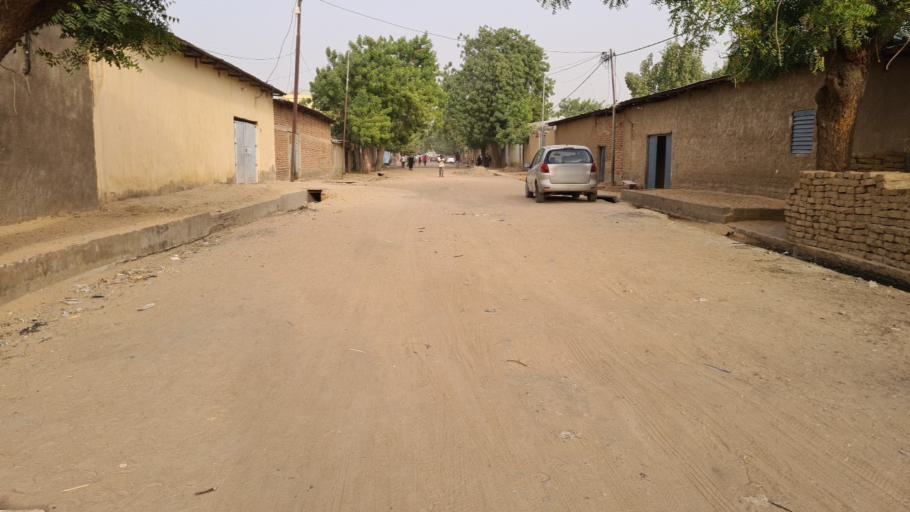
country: TD
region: Chari-Baguirmi
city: N'Djamena
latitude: 12.1037
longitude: 15.0750
